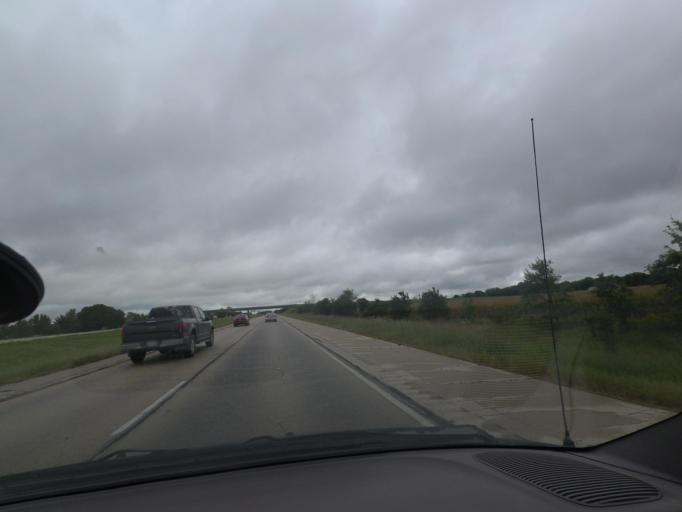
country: US
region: Illinois
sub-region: Piatt County
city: Cerro Gordo
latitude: 40.0178
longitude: -88.7293
